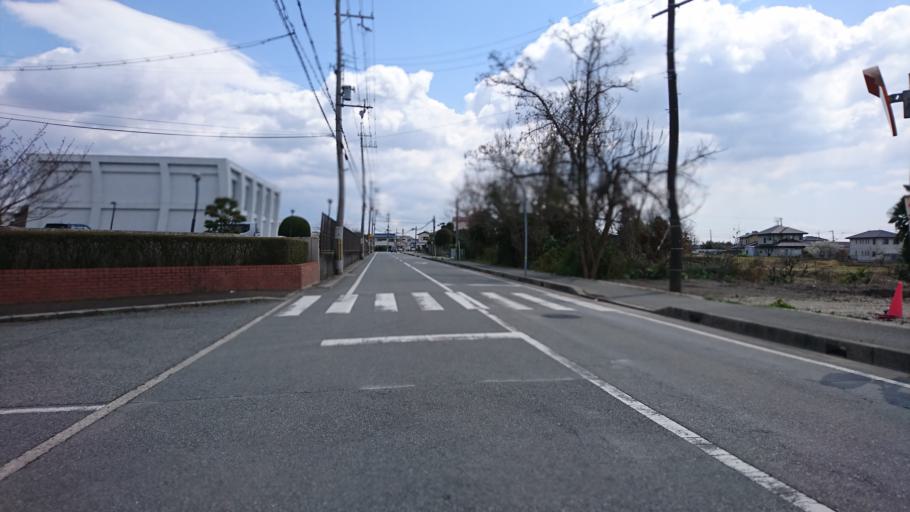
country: JP
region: Hyogo
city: Kakogawacho-honmachi
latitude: 34.7716
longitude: 134.8660
